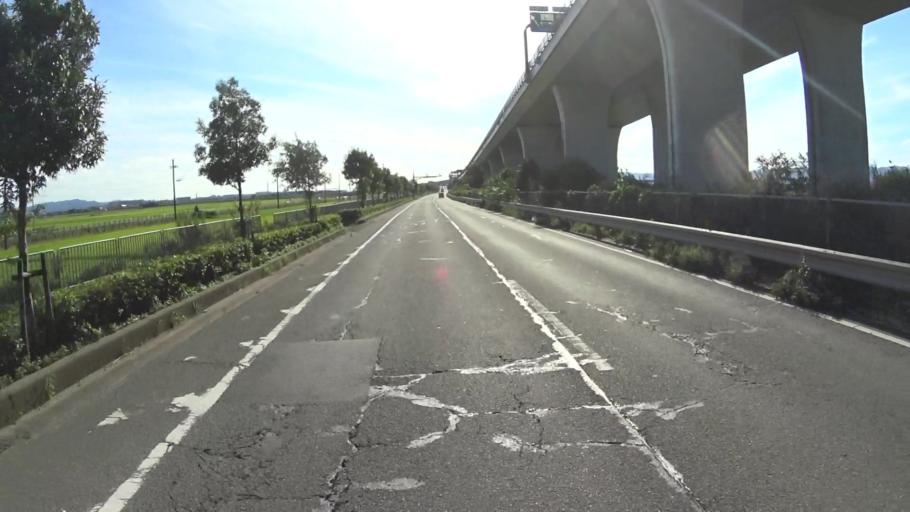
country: JP
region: Kyoto
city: Uji
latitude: 34.9011
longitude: 135.7637
